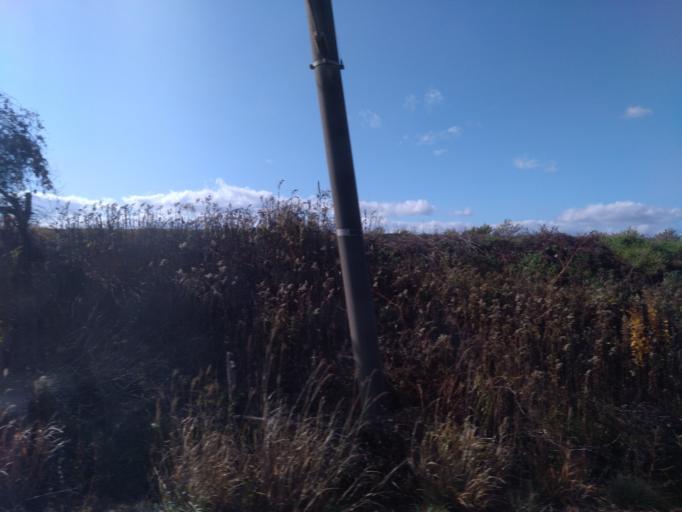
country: JP
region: Hokkaido
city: Kitahiroshima
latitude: 42.9323
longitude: 141.5725
